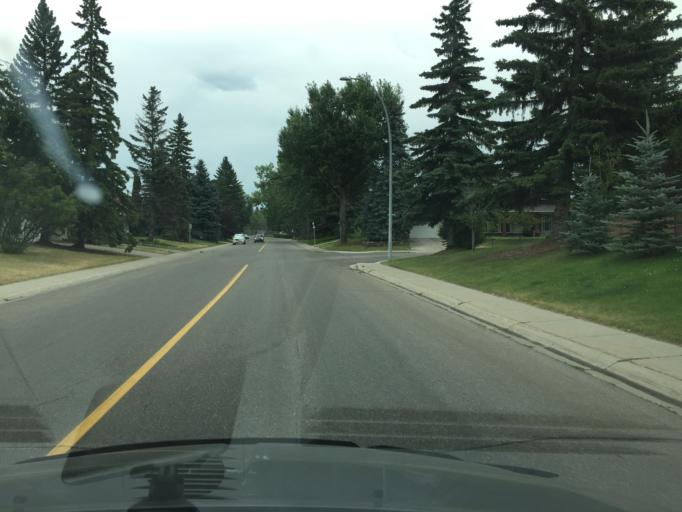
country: CA
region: Alberta
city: Calgary
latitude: 50.9456
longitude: -114.0564
